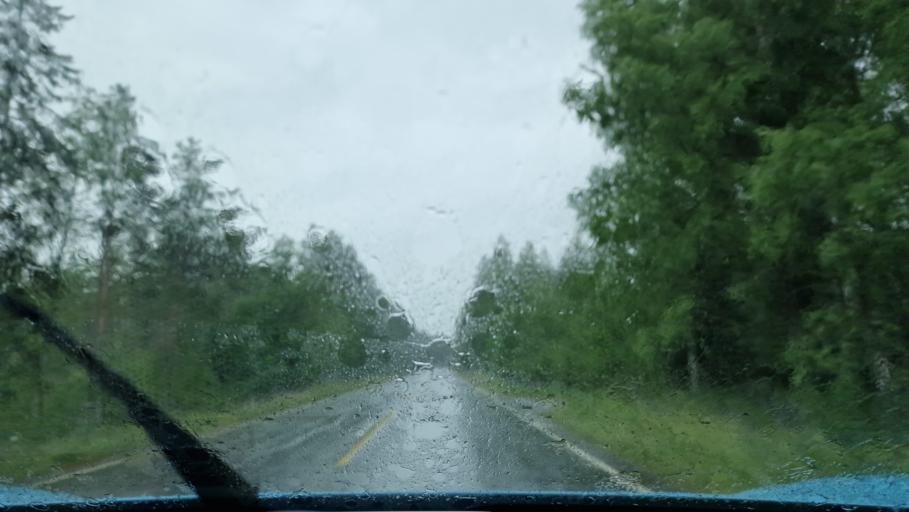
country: FI
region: Southern Ostrobothnia
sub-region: Jaerviseutu
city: Soini
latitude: 62.8331
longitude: 24.3350
